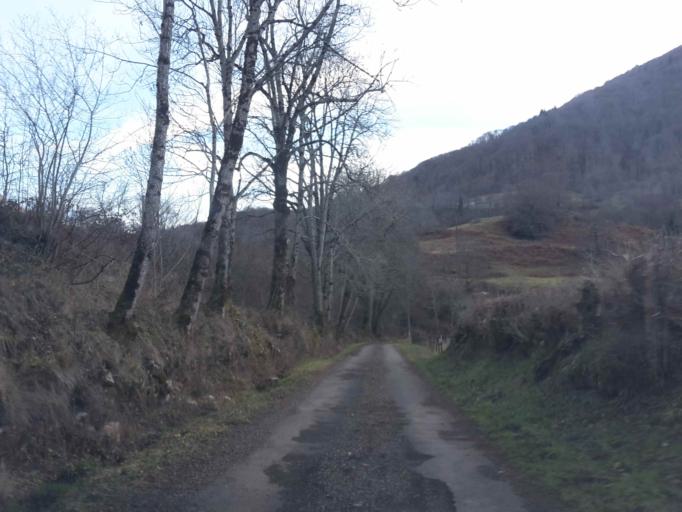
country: FR
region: Auvergne
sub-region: Departement du Cantal
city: Riom-es-Montagnes
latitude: 45.1861
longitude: 2.5705
